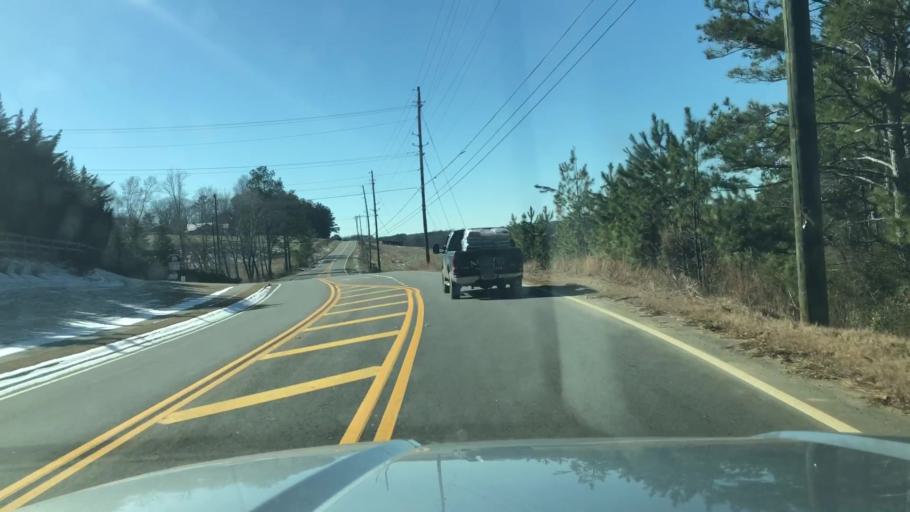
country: US
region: Georgia
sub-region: Bartow County
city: Emerson
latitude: 34.0678
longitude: -84.7937
